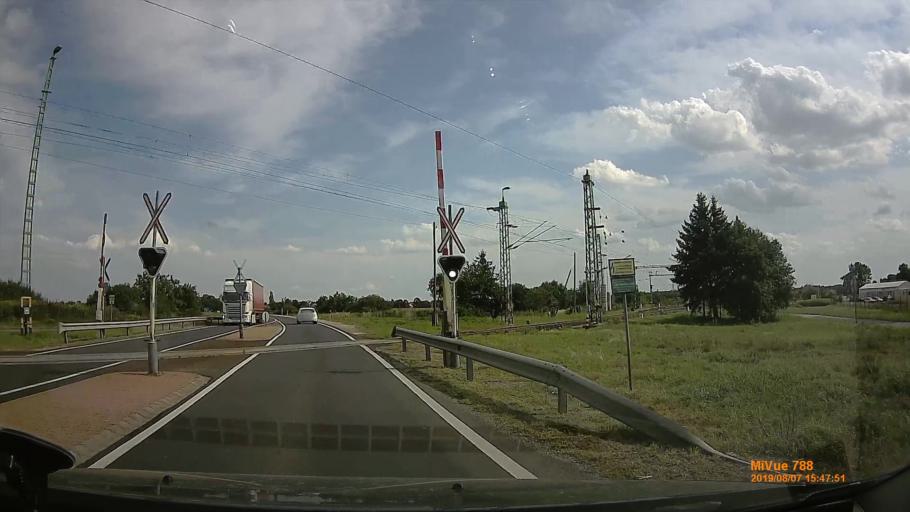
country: HU
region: Vas
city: Jak
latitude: 47.1662
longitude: 16.6313
